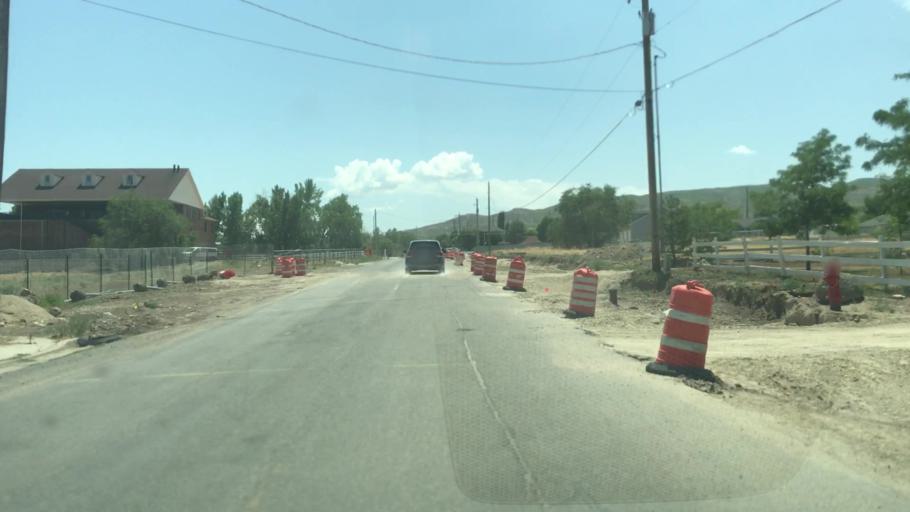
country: US
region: Utah
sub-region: Salt Lake County
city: Bluffdale
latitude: 40.4809
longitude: -111.9484
